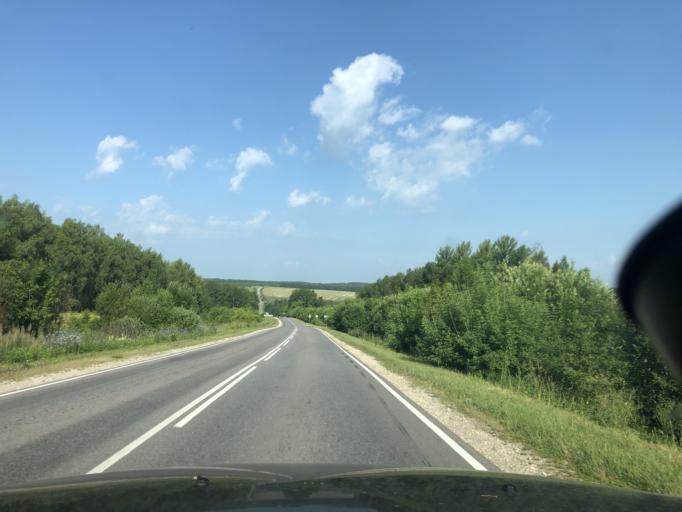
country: RU
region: Tula
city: Dubna
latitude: 54.1276
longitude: 37.0602
